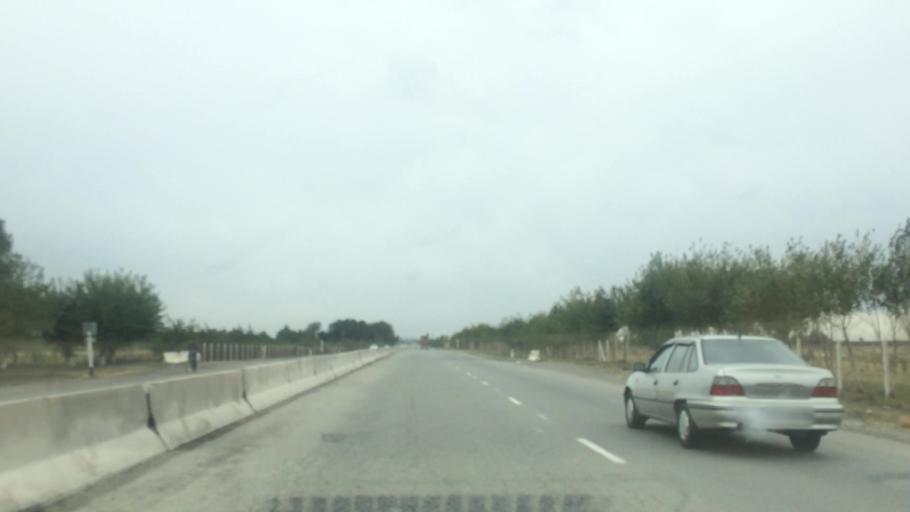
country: UZ
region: Samarqand
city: Bulung'ur
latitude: 39.7827
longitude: 67.3016
